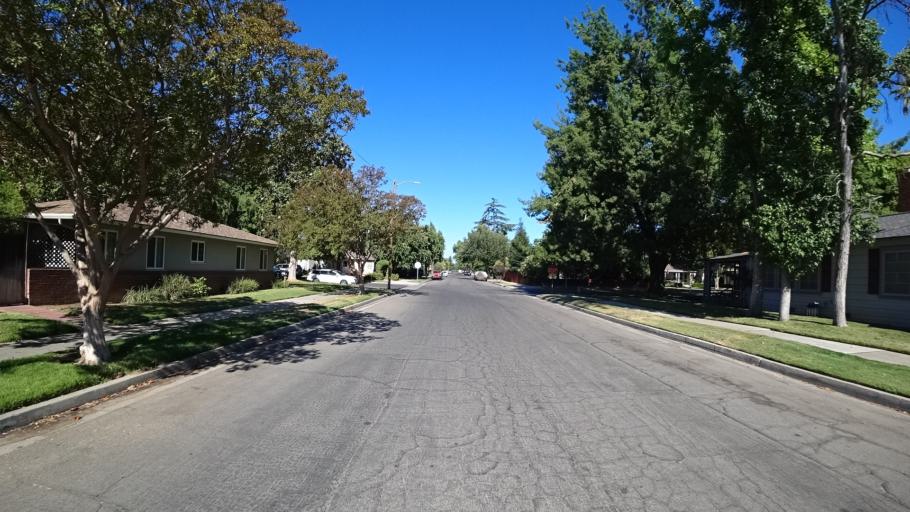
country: US
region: California
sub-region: Fresno County
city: Fresno
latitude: 36.7758
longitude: -119.8116
